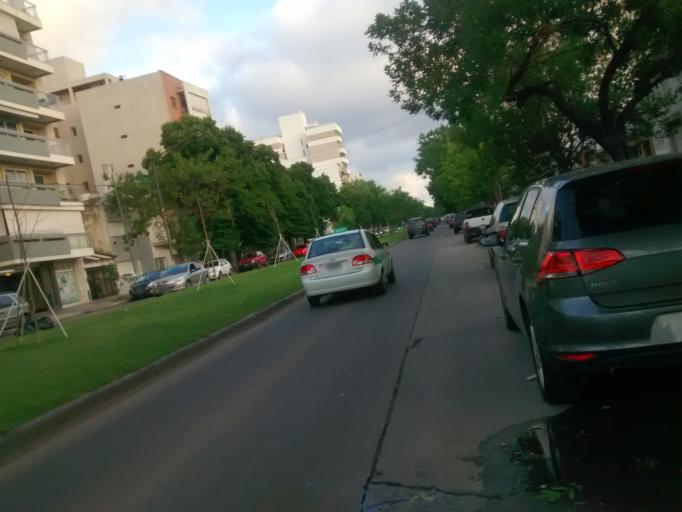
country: AR
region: Buenos Aires
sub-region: Partido de La Plata
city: La Plata
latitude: -34.9238
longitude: -57.9653
